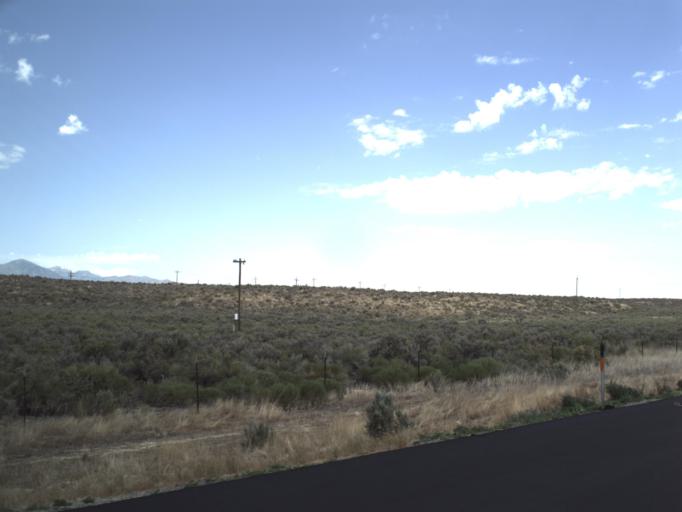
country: US
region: Utah
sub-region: Tooele County
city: Tooele
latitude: 40.1791
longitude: -112.4249
